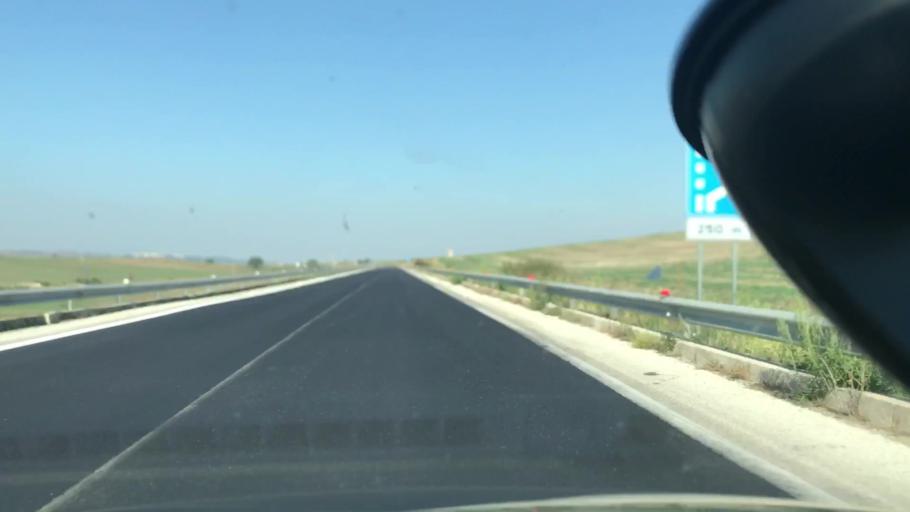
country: IT
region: Apulia
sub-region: Provincia di Barletta - Andria - Trani
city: Spinazzola
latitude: 40.9220
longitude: 16.0928
